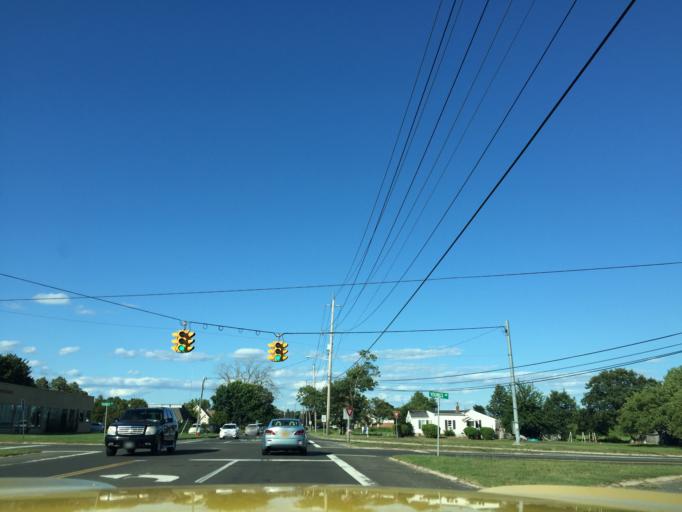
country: US
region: New York
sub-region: Suffolk County
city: Southold
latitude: 41.0720
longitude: -72.4309
